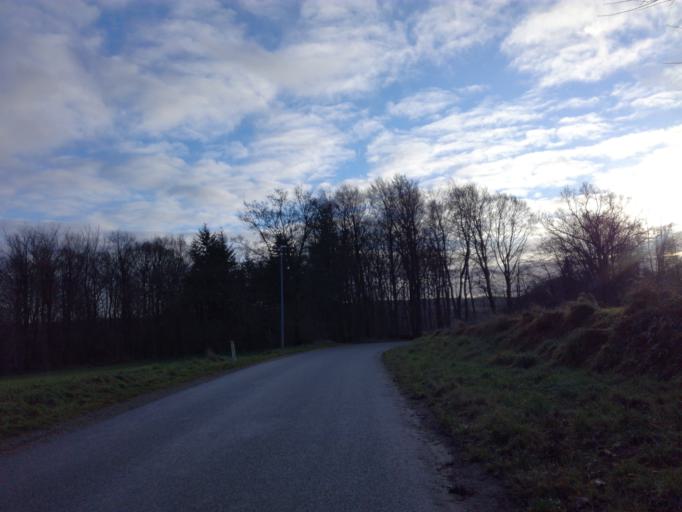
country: DK
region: South Denmark
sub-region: Fredericia Kommune
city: Taulov
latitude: 55.5528
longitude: 9.6025
